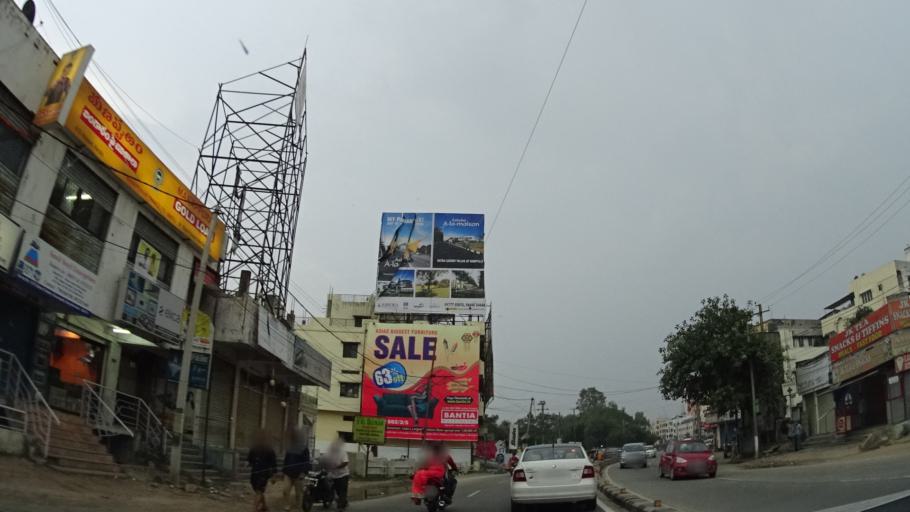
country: IN
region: Telangana
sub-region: Rangareddi
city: Quthbullapur
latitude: 17.4590
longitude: 78.4771
